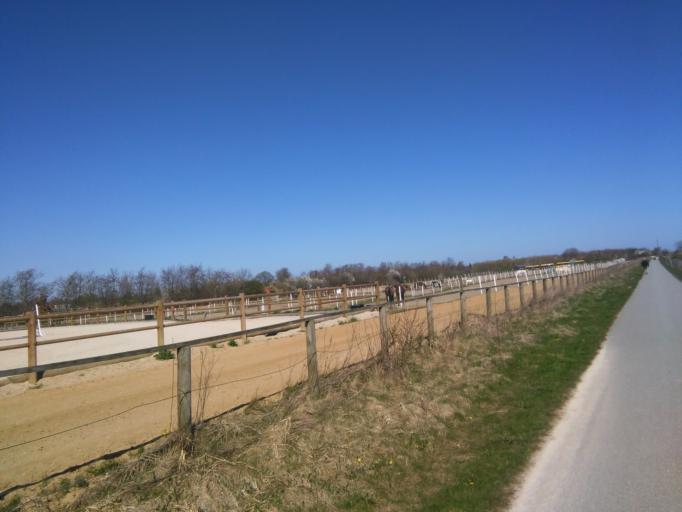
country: DK
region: Central Jutland
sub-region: Arhus Kommune
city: Marslet
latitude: 56.0817
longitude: 10.1525
